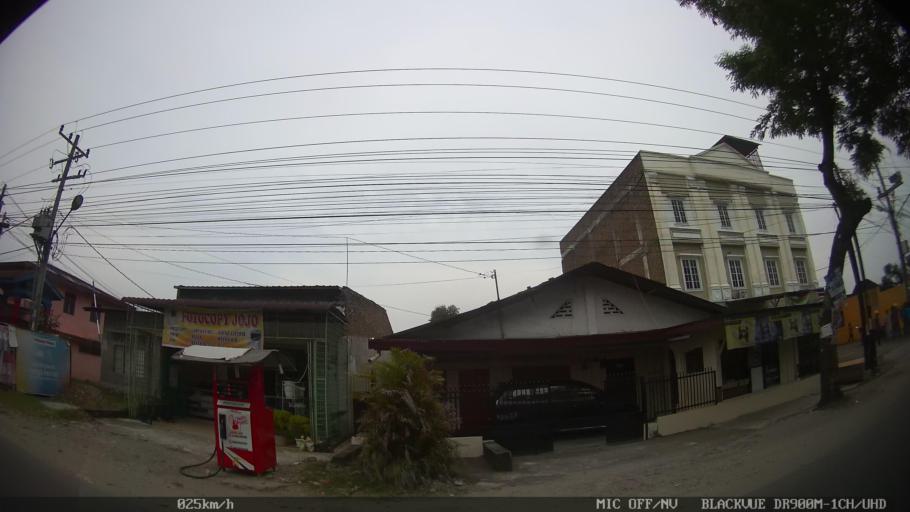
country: ID
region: North Sumatra
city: Medan
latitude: 3.5527
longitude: 98.7054
